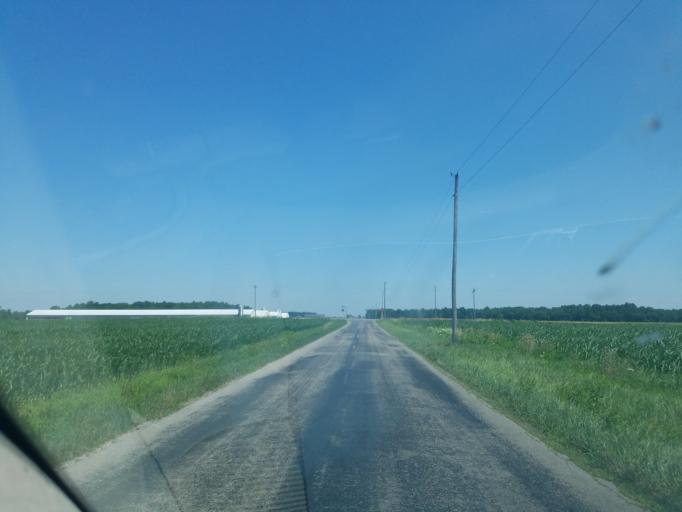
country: US
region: Ohio
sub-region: Mercer County
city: Coldwater
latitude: 40.4639
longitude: -84.7080
